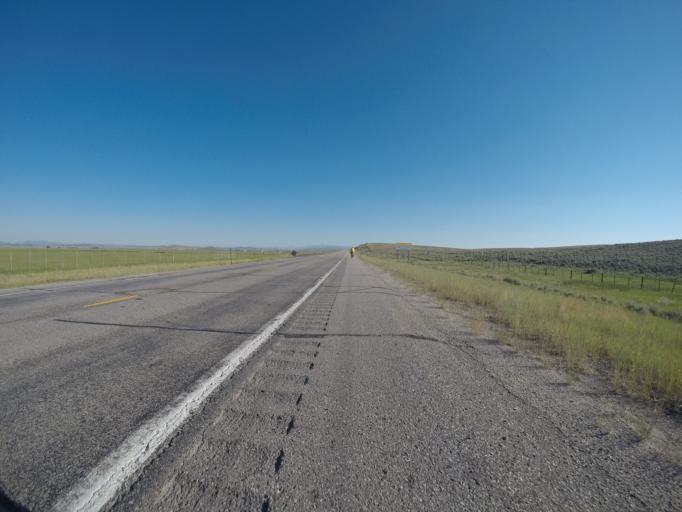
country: US
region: Wyoming
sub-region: Sublette County
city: Pinedale
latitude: 42.9371
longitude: -110.0817
